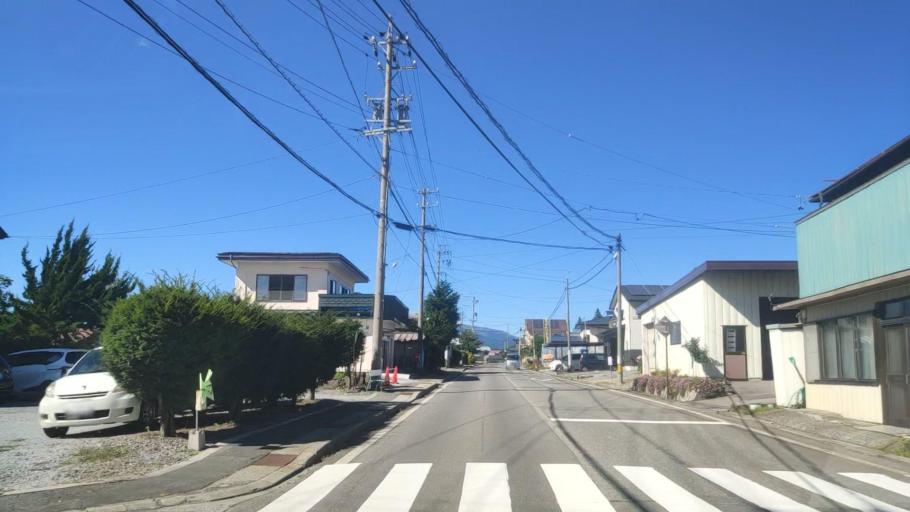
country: JP
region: Nagano
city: Chino
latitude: 35.9746
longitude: 138.2197
